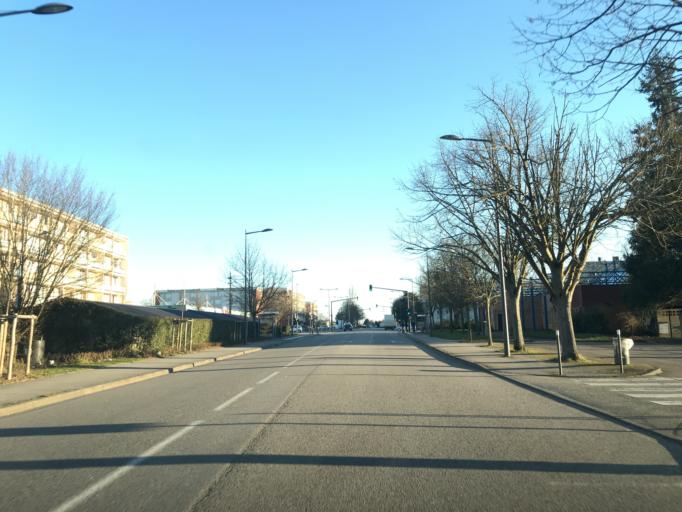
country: FR
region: Haute-Normandie
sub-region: Departement de l'Eure
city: Evreux
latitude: 49.0126
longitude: 1.1647
